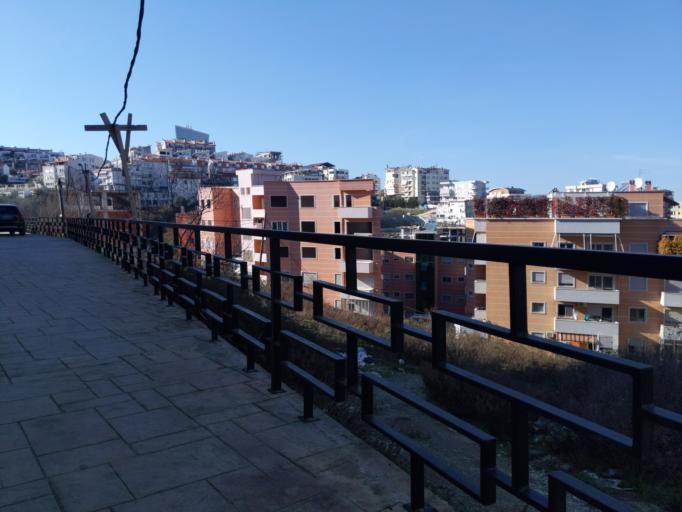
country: AL
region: Tirane
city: Tirana
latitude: 41.3080
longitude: 19.8050
